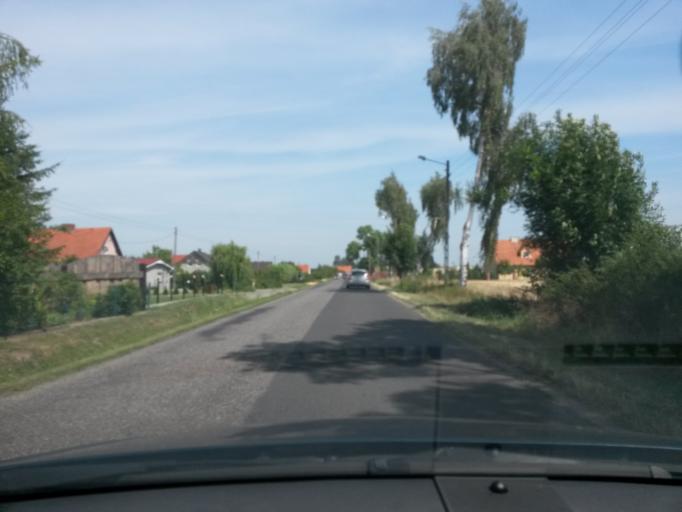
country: PL
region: Lower Silesian Voivodeship
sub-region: Powiat legnicki
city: Prochowice
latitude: 51.2574
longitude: 16.3640
